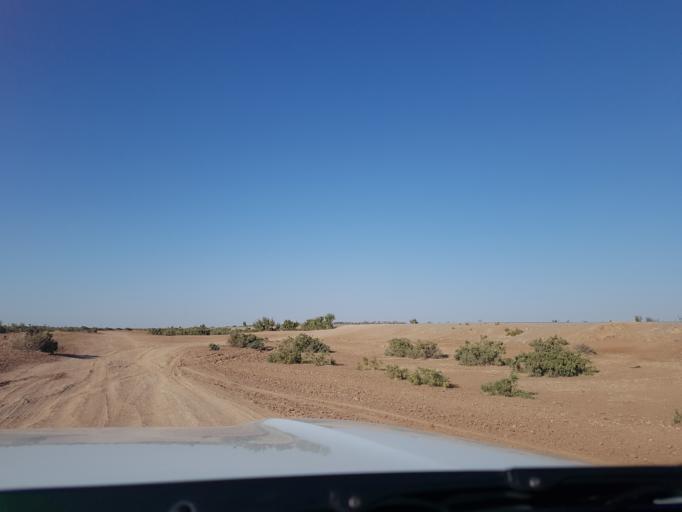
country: IR
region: Razavi Khorasan
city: Sarakhs
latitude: 36.9897
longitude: 61.3878
